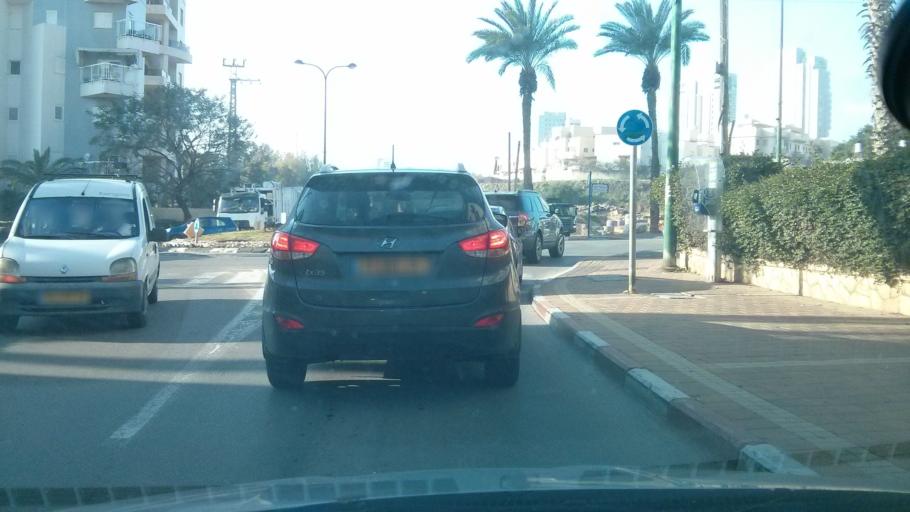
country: IL
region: Central District
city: Netanya
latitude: 32.3192
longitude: 34.8510
